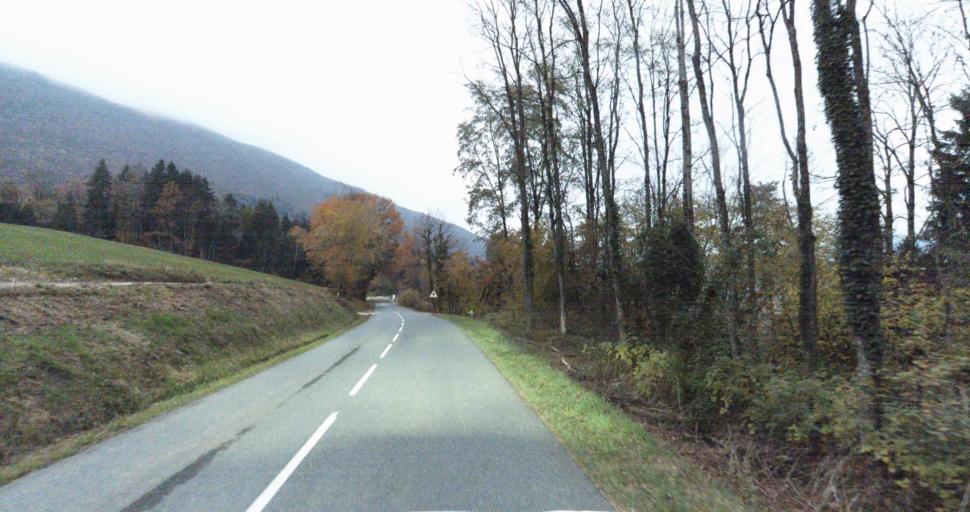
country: FR
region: Rhone-Alpes
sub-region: Departement de la Haute-Savoie
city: Saint-Jorioz
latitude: 45.8368
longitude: 6.1416
